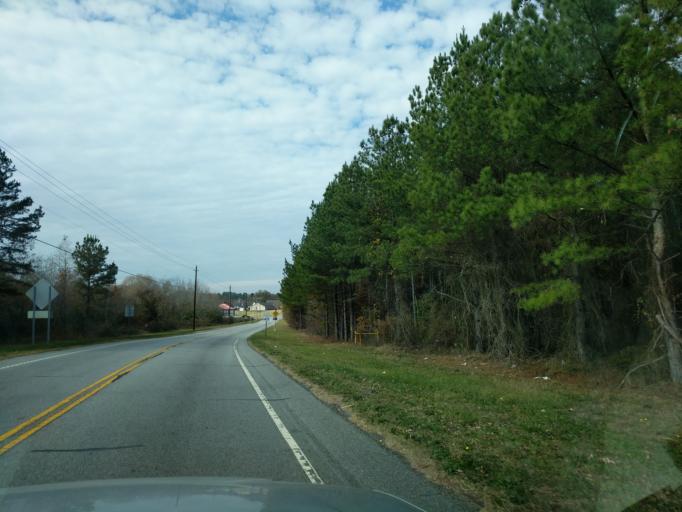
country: US
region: South Carolina
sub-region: Anderson County
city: Piedmont
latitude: 34.7103
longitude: -82.5051
